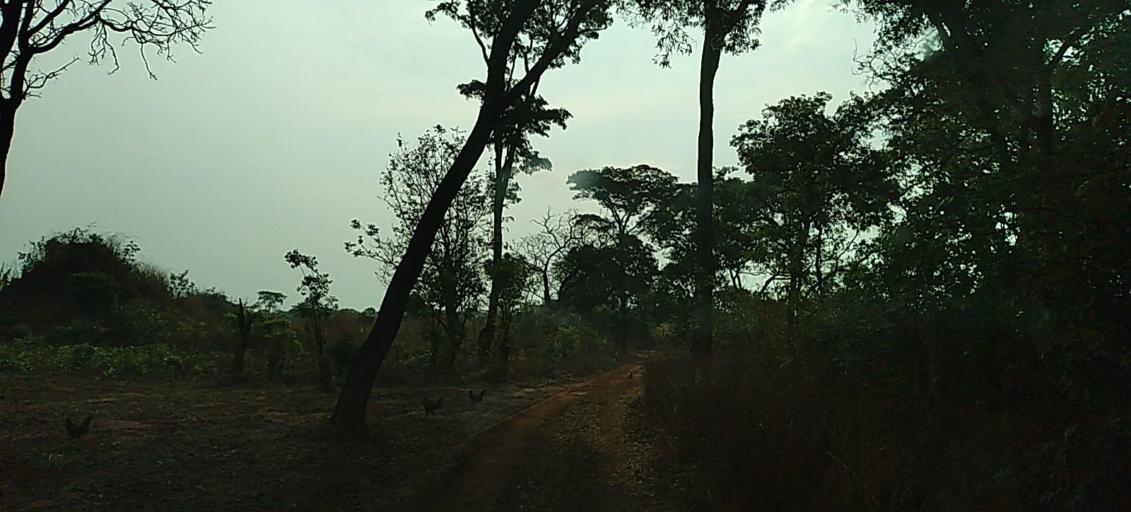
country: ZM
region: North-Western
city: Solwezi
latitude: -12.0550
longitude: 26.1543
